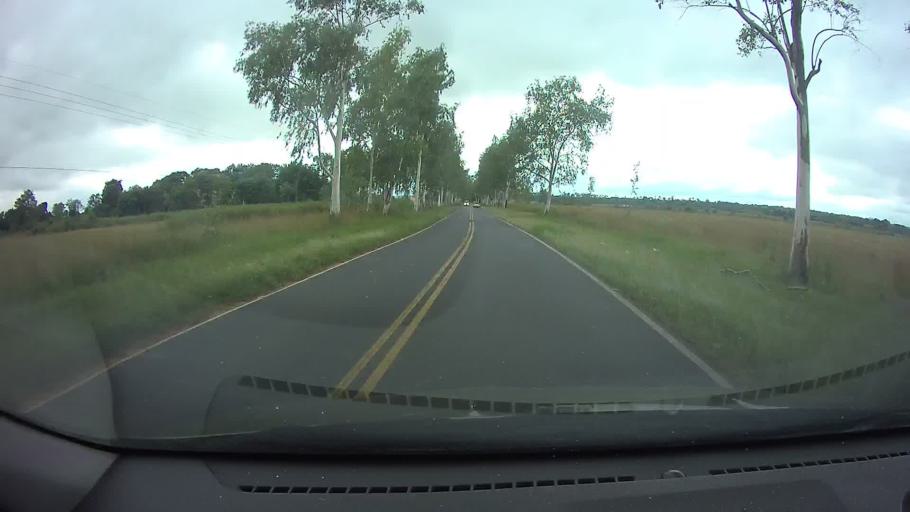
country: PY
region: Central
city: Nueva Italia
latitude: -25.5541
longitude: -57.5025
